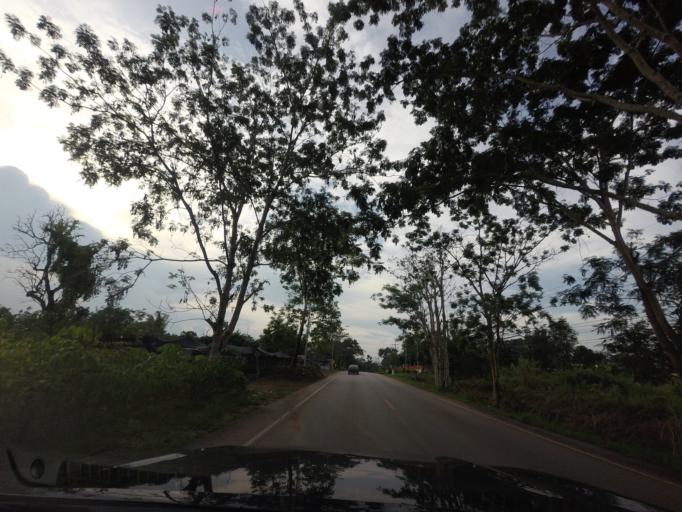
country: TH
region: Changwat Udon Thani
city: Nam Som
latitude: 17.8369
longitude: 102.2592
